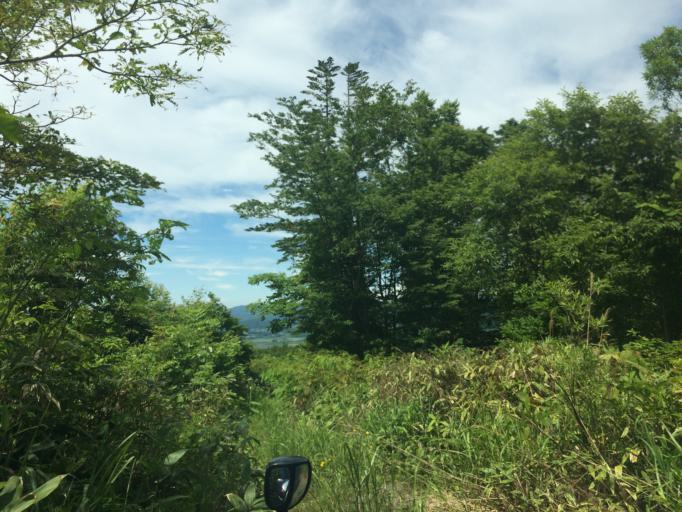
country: JP
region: Hokkaido
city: Niseko Town
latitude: 42.8626
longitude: 140.8196
